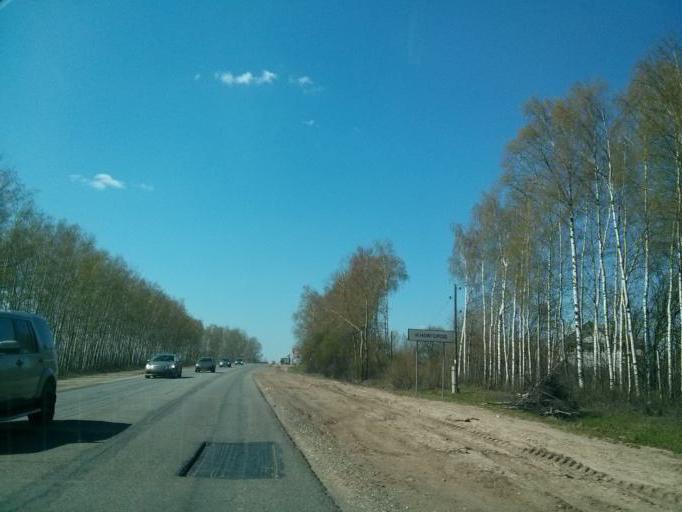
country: RU
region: Nizjnij Novgorod
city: Nizhniy Novgorod
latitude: 56.2162
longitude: 43.9500
